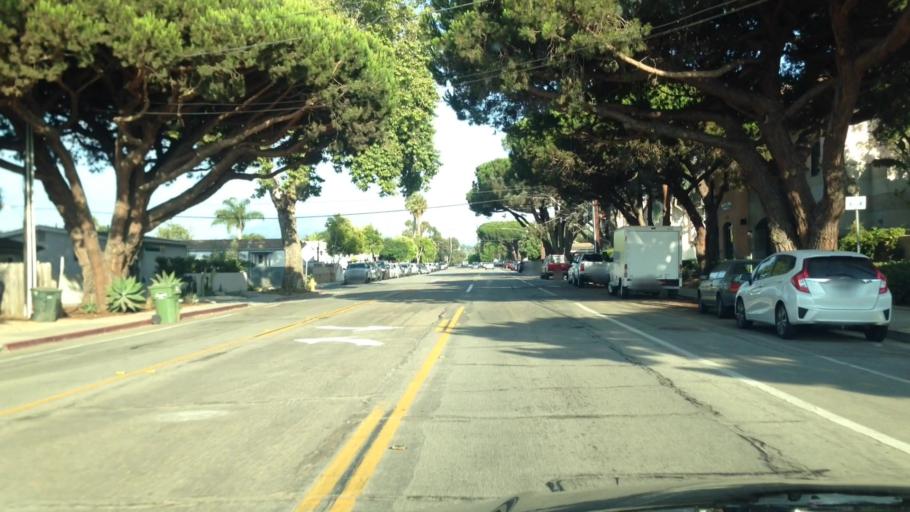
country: US
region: California
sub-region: Santa Barbara County
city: Carpinteria
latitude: 34.4033
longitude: -119.5320
